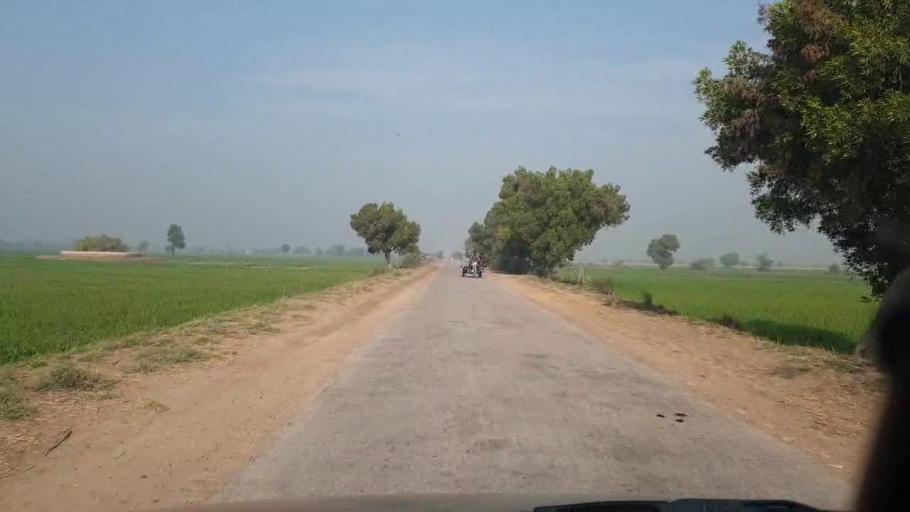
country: PK
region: Sindh
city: Shahdadpur
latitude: 25.9809
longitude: 68.5716
